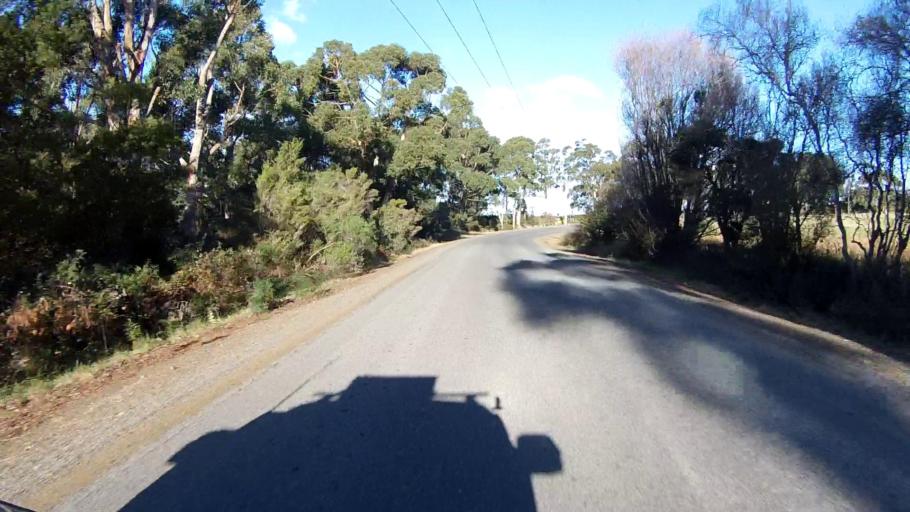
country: AU
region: Tasmania
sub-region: Clarence
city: Sandford
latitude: -43.1658
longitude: 147.8594
